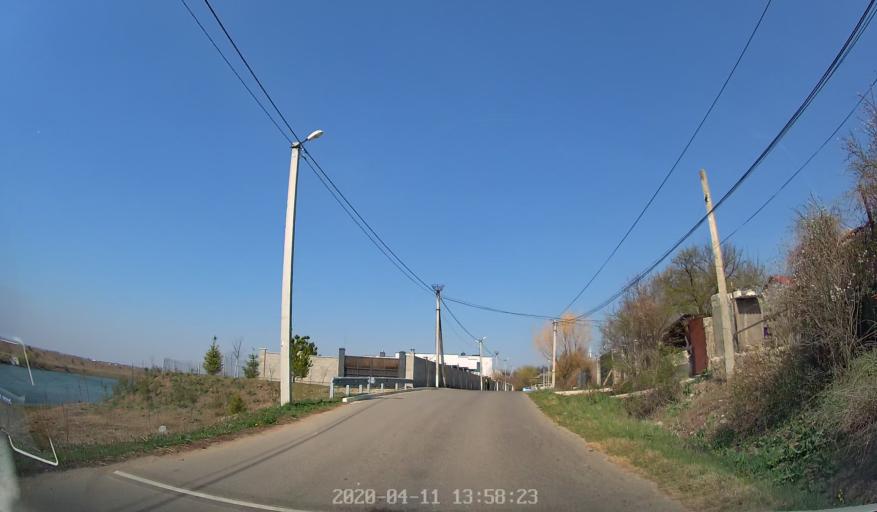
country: MD
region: Chisinau
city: Vadul lui Voda
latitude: 47.0788
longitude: 29.1295
